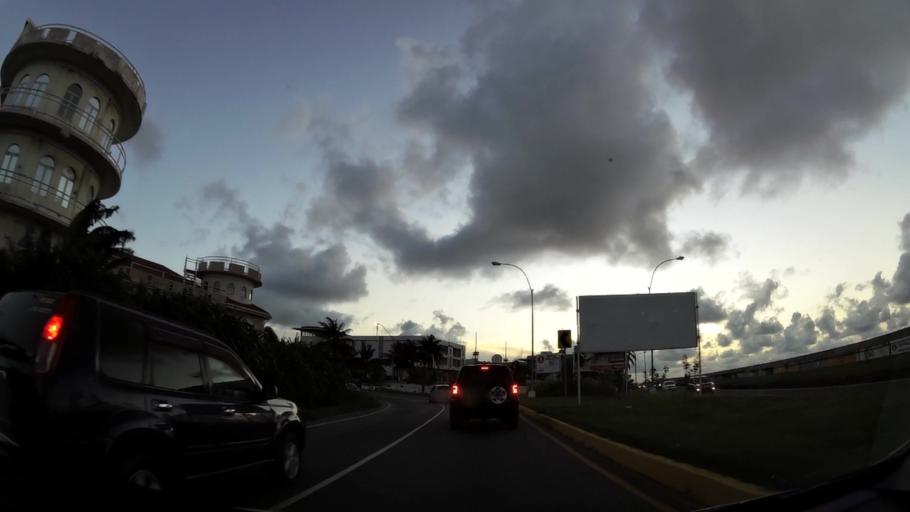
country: GY
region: Demerara-Mahaica
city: Georgetown
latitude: 6.8250
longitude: -58.1365
